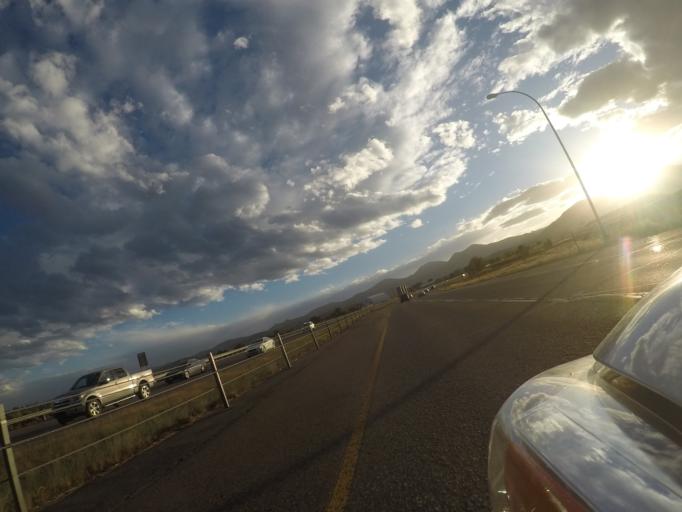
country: US
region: Colorado
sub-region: Jefferson County
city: Ken Caryl
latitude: 39.6410
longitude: -105.1356
